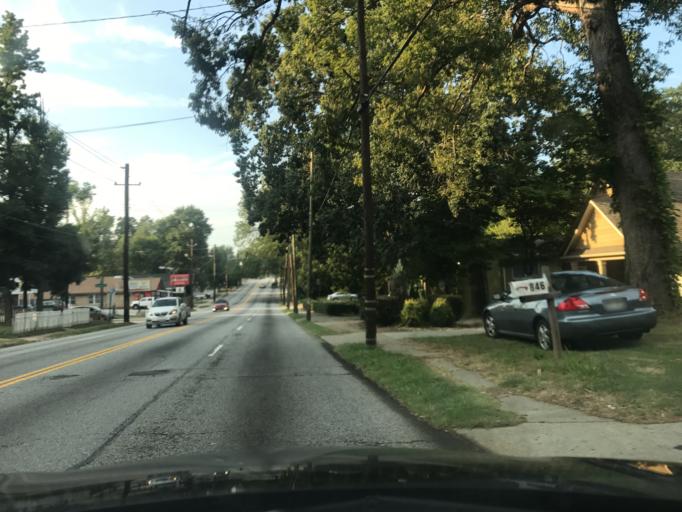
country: US
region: Georgia
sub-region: Fulton County
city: Atlanta
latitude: 33.7312
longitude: -84.3493
